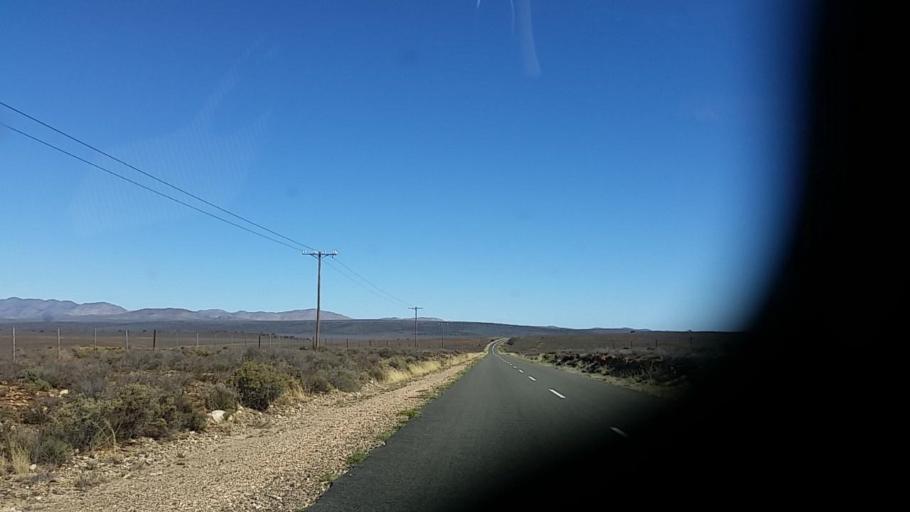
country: ZA
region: Eastern Cape
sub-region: Cacadu District Municipality
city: Willowmore
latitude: -33.5242
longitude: 23.1084
